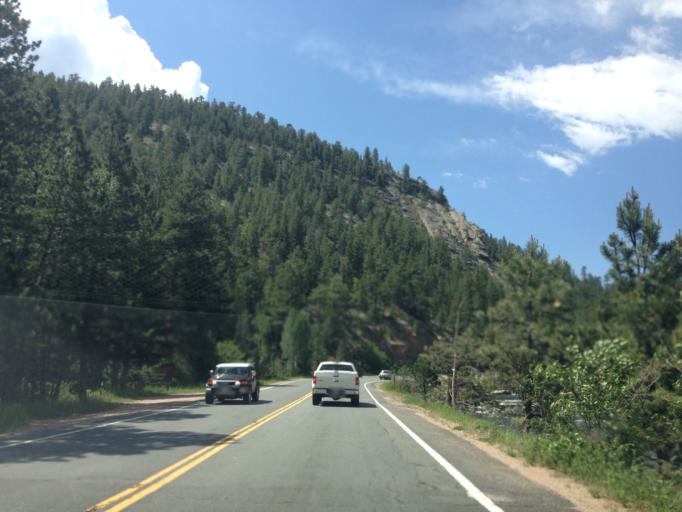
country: US
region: Colorado
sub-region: Larimer County
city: Estes Park
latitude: 40.3823
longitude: -105.4705
